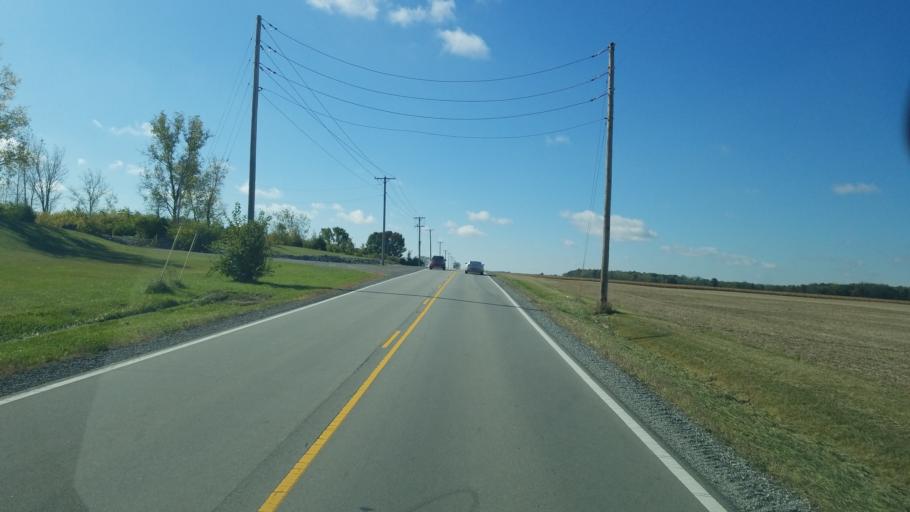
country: US
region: Ohio
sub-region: Highland County
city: Leesburg
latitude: 39.4251
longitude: -83.5172
